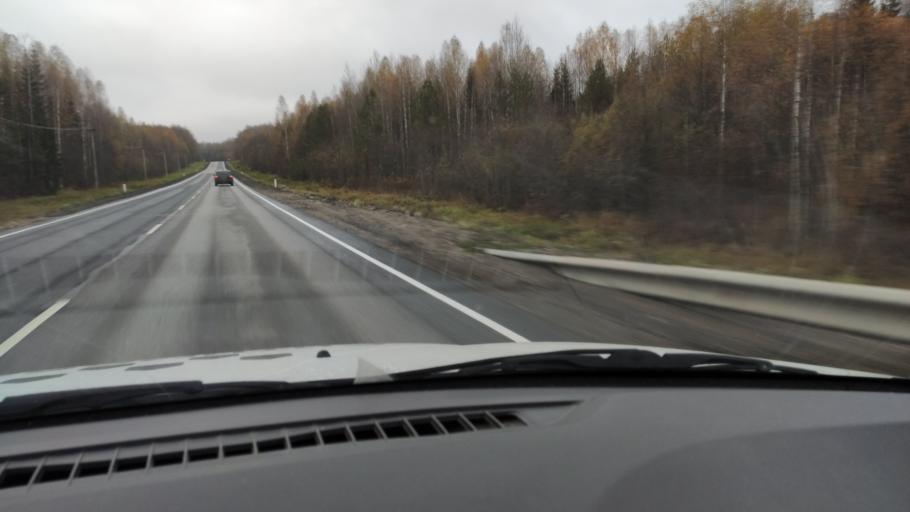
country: RU
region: Kirov
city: Belaya Kholunitsa
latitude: 58.9195
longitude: 51.1272
